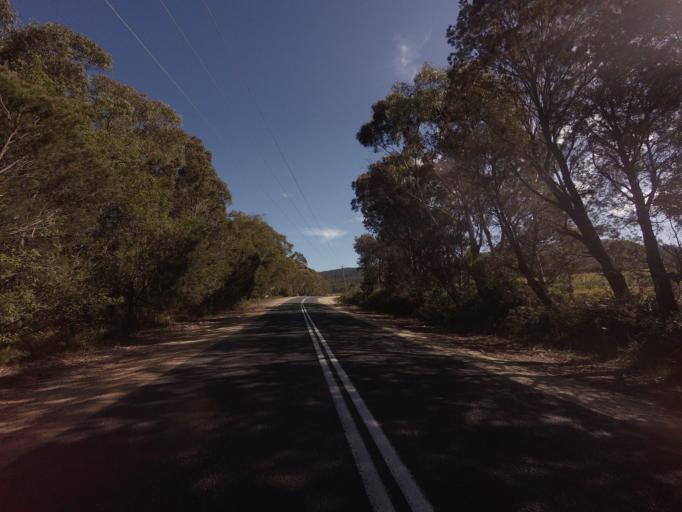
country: AU
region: Tasmania
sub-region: Break O'Day
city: St Helens
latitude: -41.8317
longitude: 148.2582
